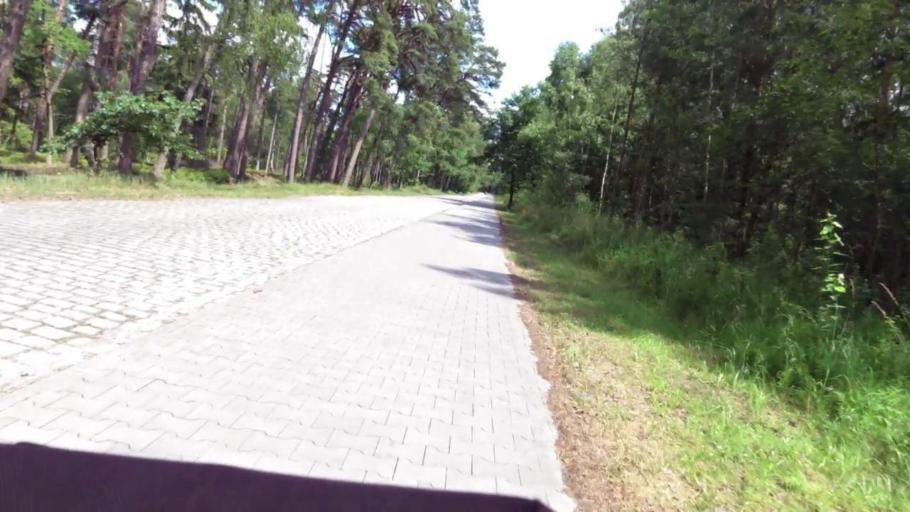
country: PL
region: West Pomeranian Voivodeship
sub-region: Powiat gryficki
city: Mrzezyno
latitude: 54.1320
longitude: 15.2615
